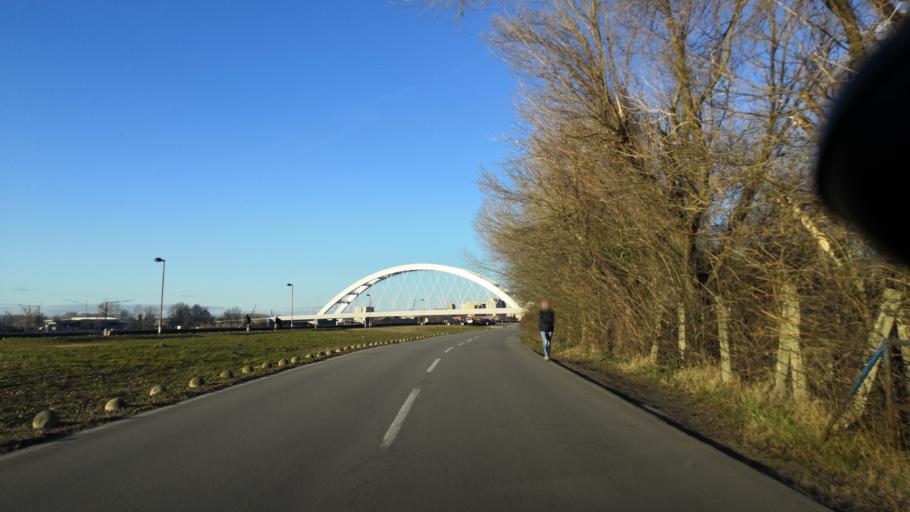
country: RS
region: Autonomna Pokrajina Vojvodina
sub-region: Juznobacki Okrug
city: Petrovaradin
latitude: 45.2568
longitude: 19.8591
